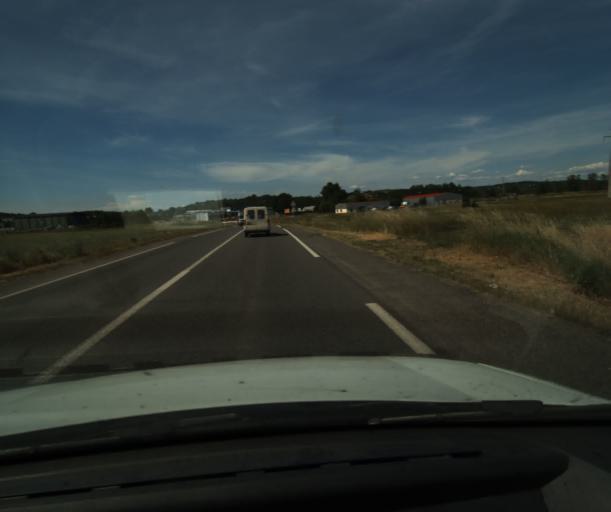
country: FR
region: Midi-Pyrenees
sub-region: Departement du Tarn-et-Garonne
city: Moissac
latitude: 44.1048
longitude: 1.1135
